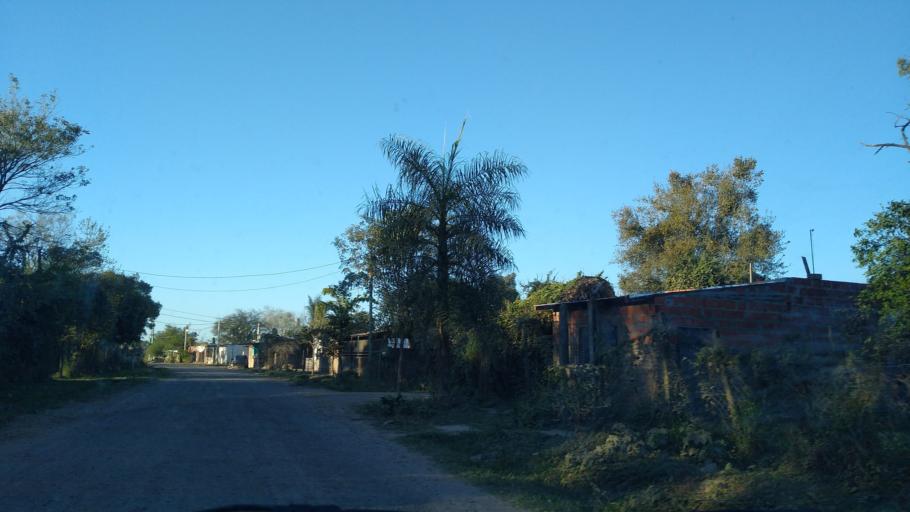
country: AR
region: Chaco
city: Barranqueras
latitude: -27.4738
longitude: -58.9472
